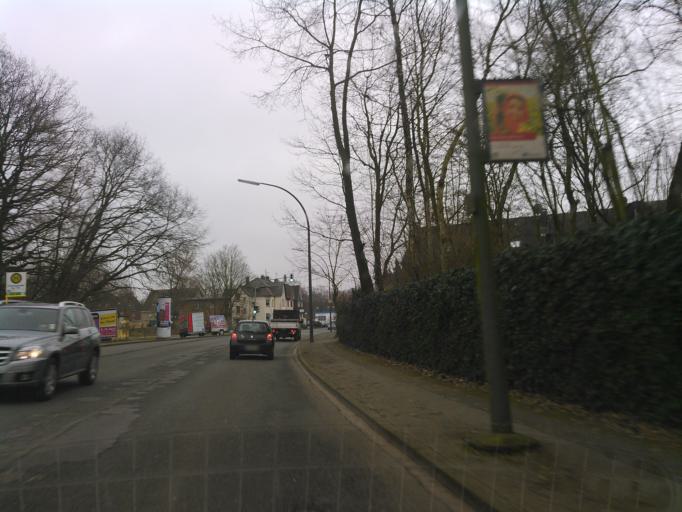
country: DE
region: North Rhine-Westphalia
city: Marl
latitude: 51.6669
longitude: 7.1476
